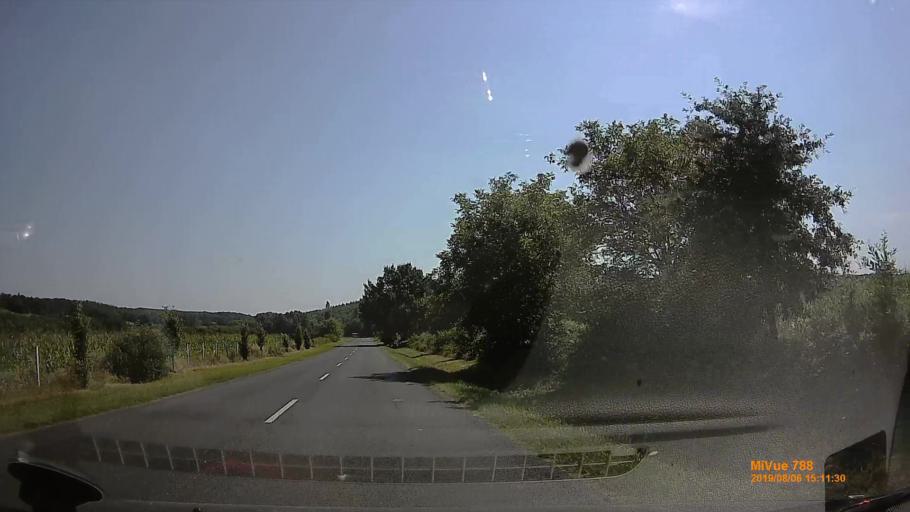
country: HU
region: Zala
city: Nagykanizsa
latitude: 46.3773
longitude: 16.9768
